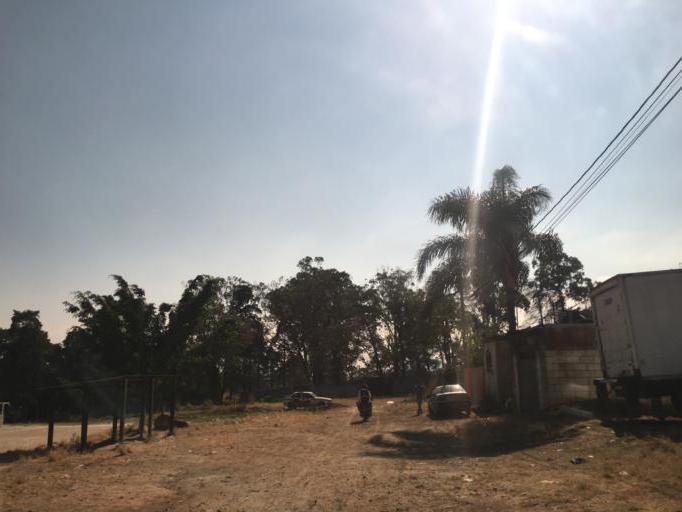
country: GT
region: Guatemala
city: Mixco
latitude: 14.6083
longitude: -90.5750
